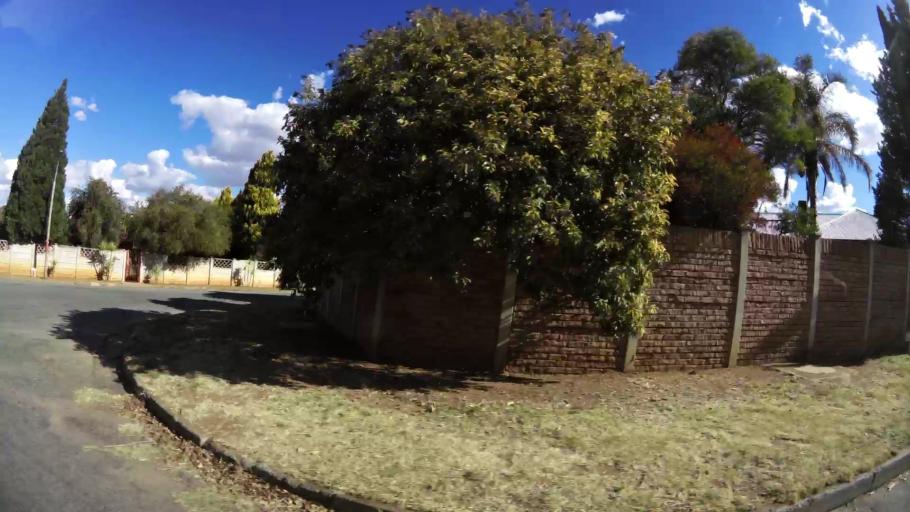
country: ZA
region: North-West
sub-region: Dr Kenneth Kaunda District Municipality
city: Klerksdorp
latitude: -26.8622
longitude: 26.6485
